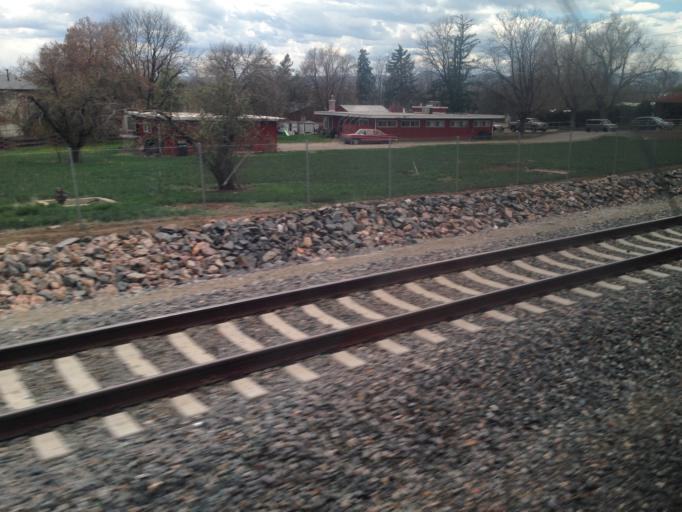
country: US
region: Colorado
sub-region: Jefferson County
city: Arvada
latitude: 39.7933
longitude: -105.1042
